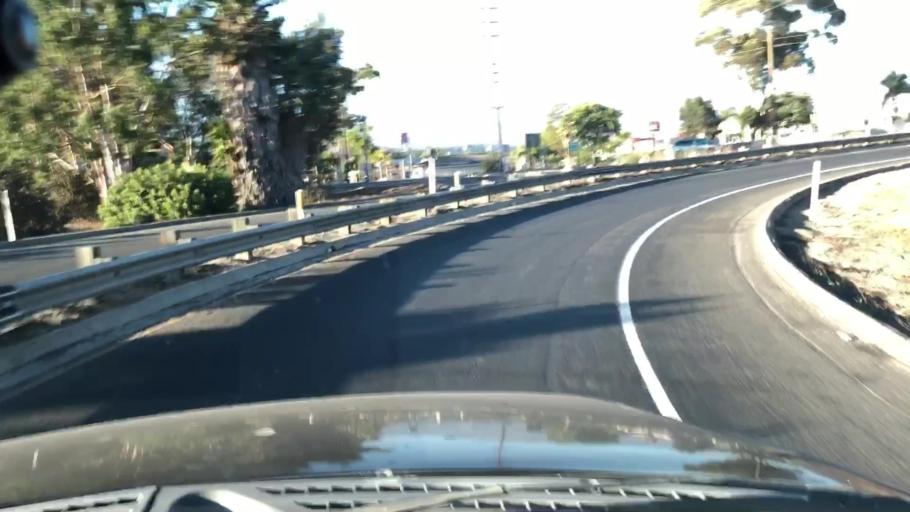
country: US
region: California
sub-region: Ventura County
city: Saticoy
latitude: 34.2900
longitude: -119.1578
